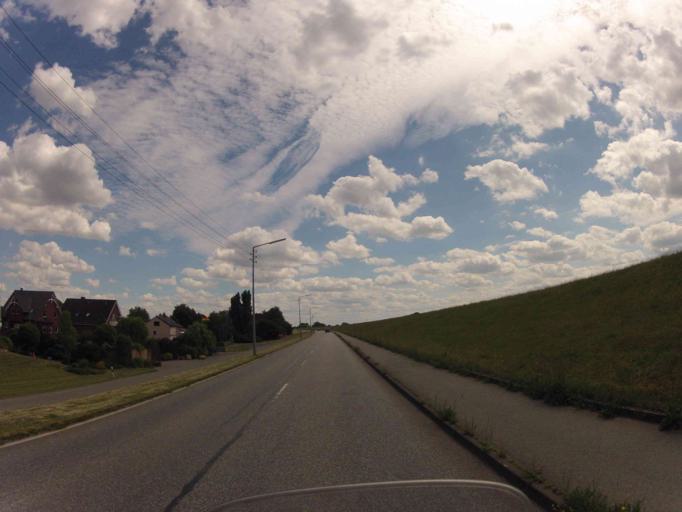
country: DE
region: Hamburg
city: Rothenburgsort
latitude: 53.4844
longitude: 10.0554
